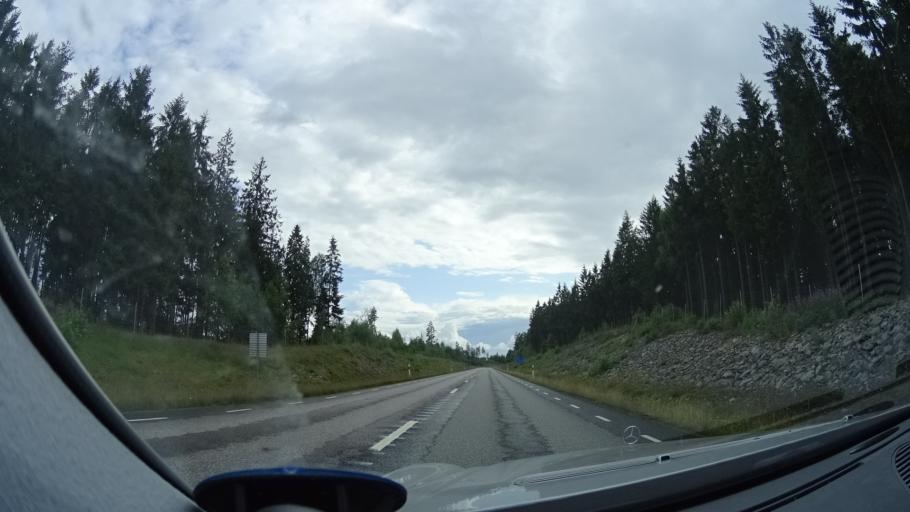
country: SE
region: Blekinge
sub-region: Karlshamns Kommun
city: Svangsta
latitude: 56.2788
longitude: 14.8649
